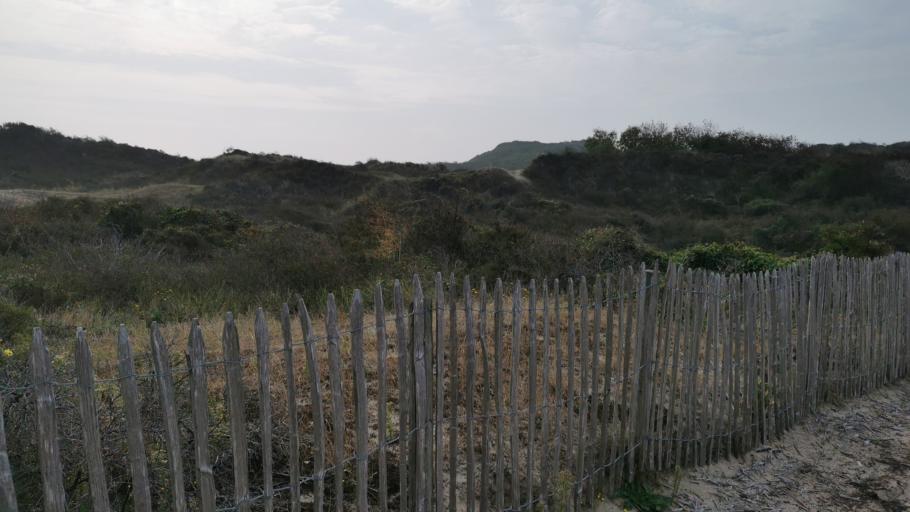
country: FR
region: Picardie
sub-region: Departement de la Somme
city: Fort-Mahon-Plage
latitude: 50.3360
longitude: 1.5552
